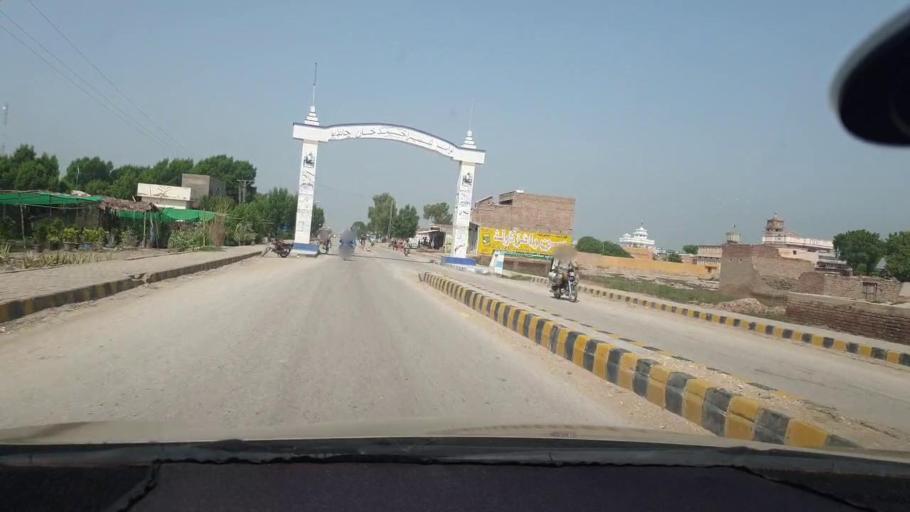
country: PK
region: Sindh
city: Kambar
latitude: 27.5883
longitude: 68.0232
